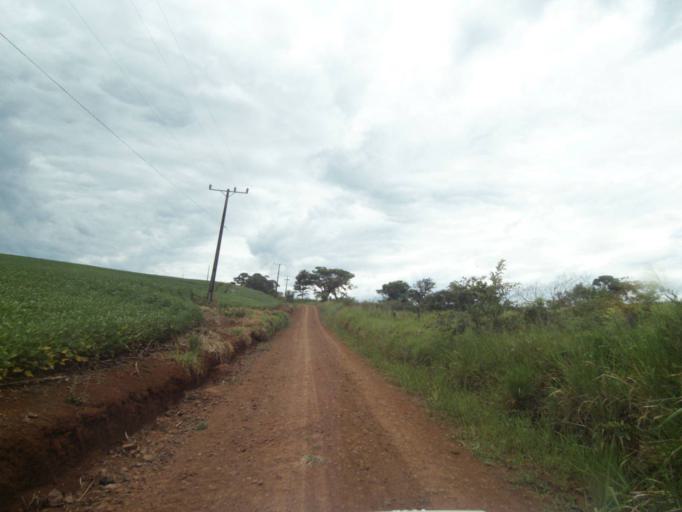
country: BR
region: Parana
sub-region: Guaraniacu
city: Guaraniacu
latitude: -24.9270
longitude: -52.9376
